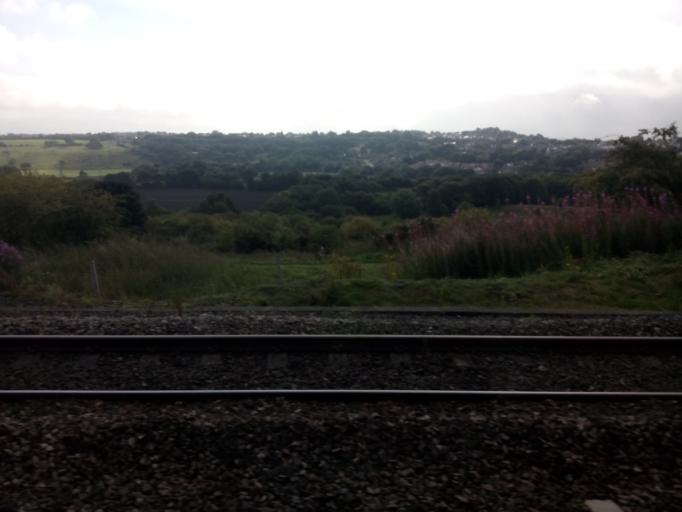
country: GB
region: England
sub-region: County Durham
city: Durham
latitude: 54.7850
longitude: -1.5785
